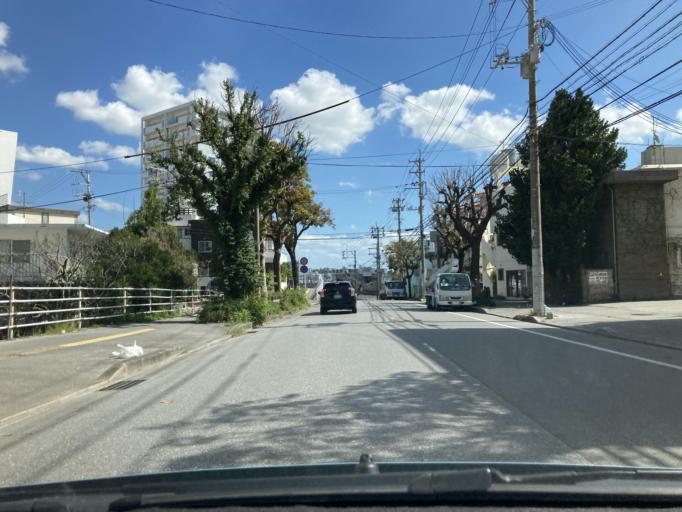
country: JP
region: Okinawa
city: Naha-shi
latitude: 26.2061
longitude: 127.6871
